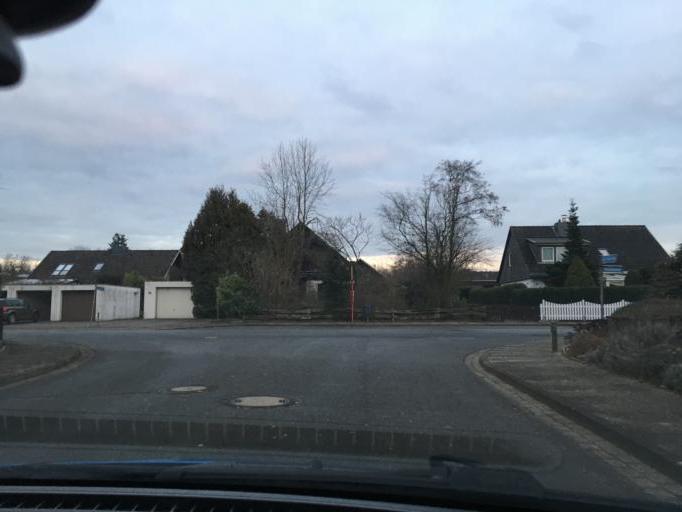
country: DE
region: Lower Saxony
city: Wendisch Evern
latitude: 53.2288
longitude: 10.4438
